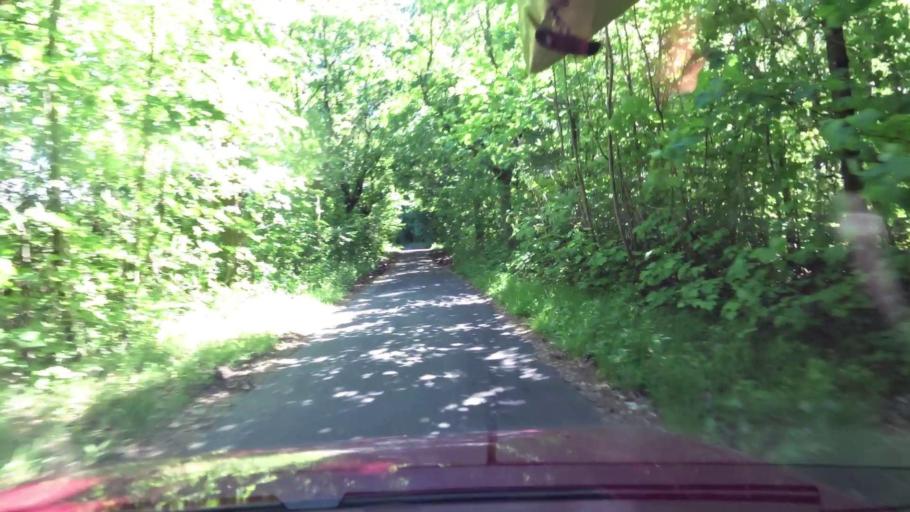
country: PL
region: West Pomeranian Voivodeship
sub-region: Powiat koszalinski
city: Polanow
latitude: 54.0355
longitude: 16.7840
